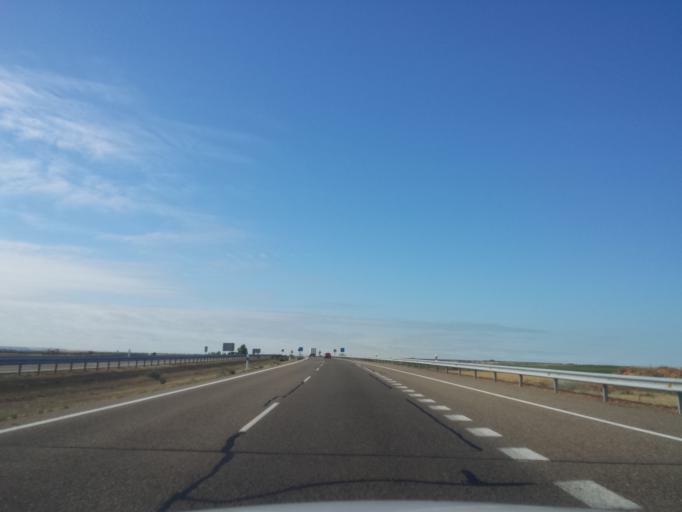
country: ES
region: Castille and Leon
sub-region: Provincia de Leon
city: Ardon
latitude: 42.4337
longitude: -5.5861
